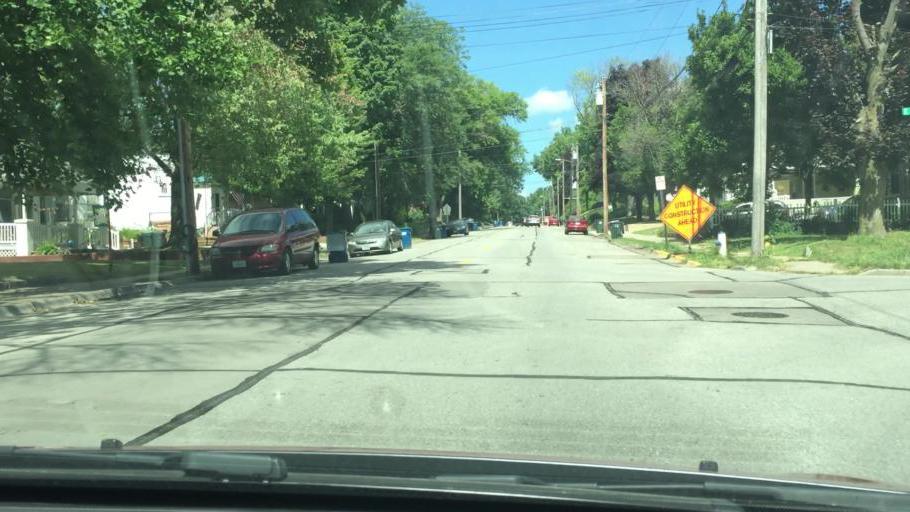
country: US
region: Iowa
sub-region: Muscatine County
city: Muscatine
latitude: 41.4307
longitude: -91.0486
